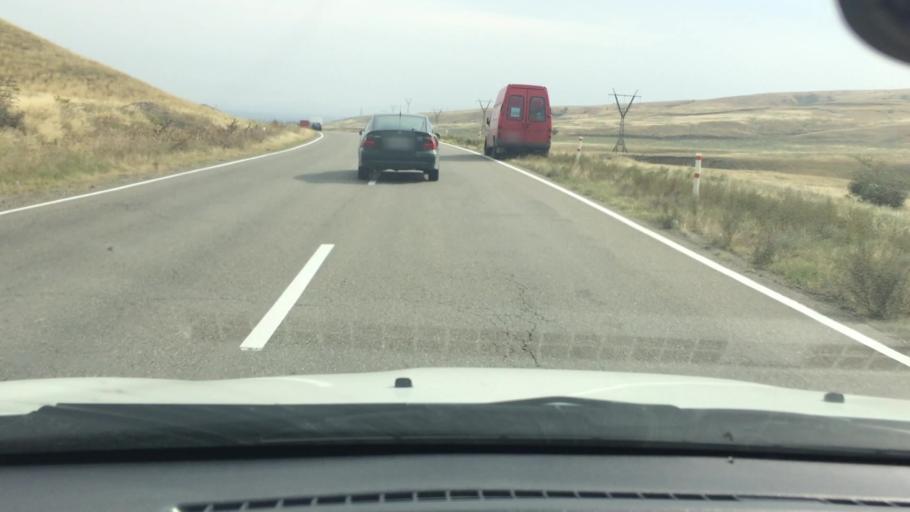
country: GE
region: Kvemo Kartli
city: Rust'avi
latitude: 41.5028
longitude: 44.9548
